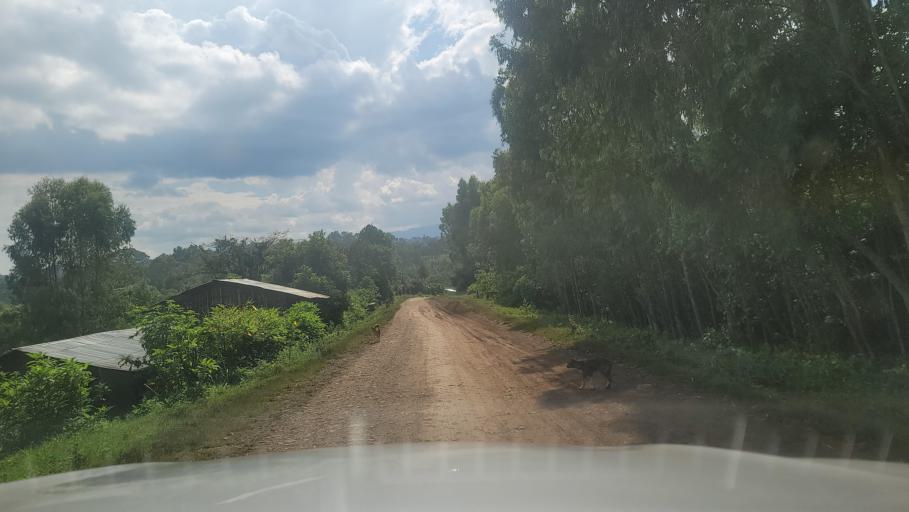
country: ET
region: Oromiya
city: Agaro
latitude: 7.7293
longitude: 36.2591
